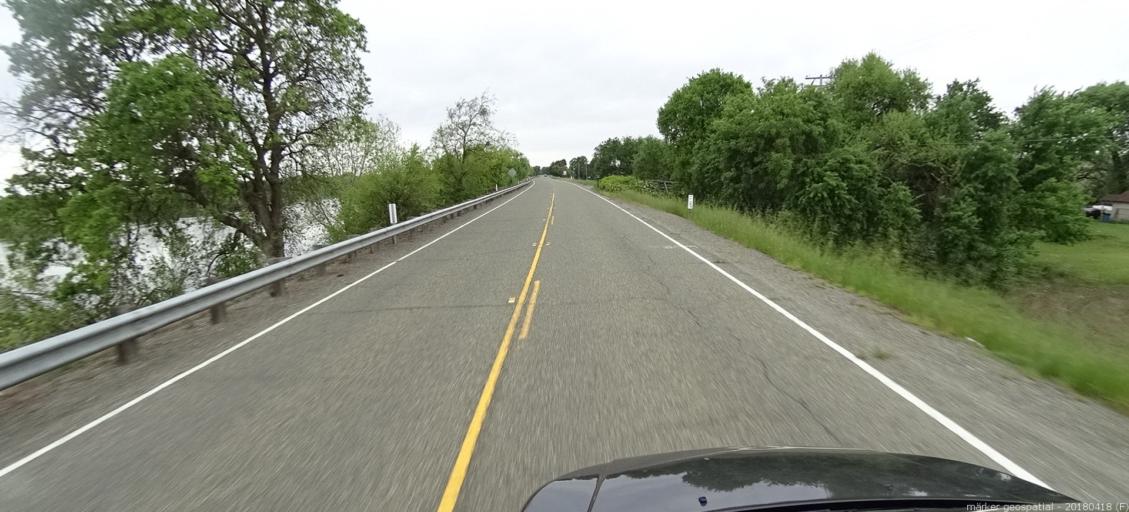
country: US
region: California
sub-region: Sacramento County
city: Laguna
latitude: 38.4105
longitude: -121.5170
